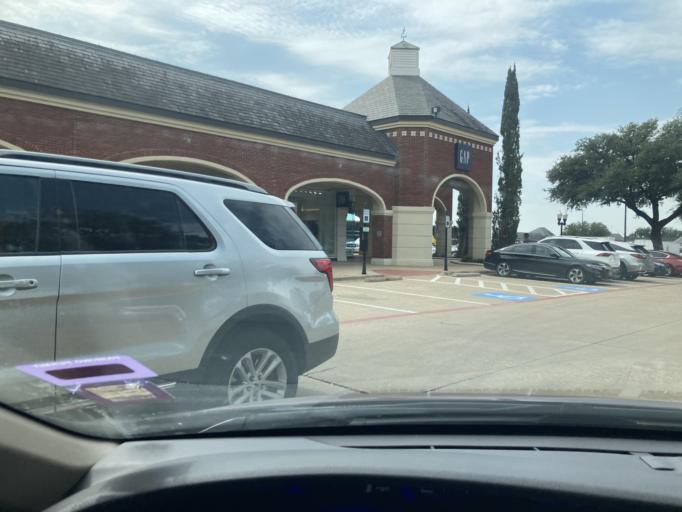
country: US
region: Texas
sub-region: Dallas County
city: Addison
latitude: 33.0262
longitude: -96.7906
